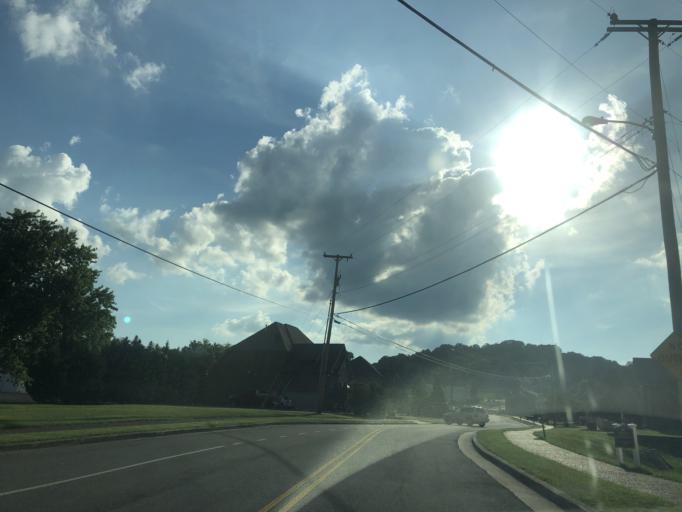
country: US
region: Tennessee
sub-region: Davidson County
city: Nashville
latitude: 36.2551
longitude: -86.8303
